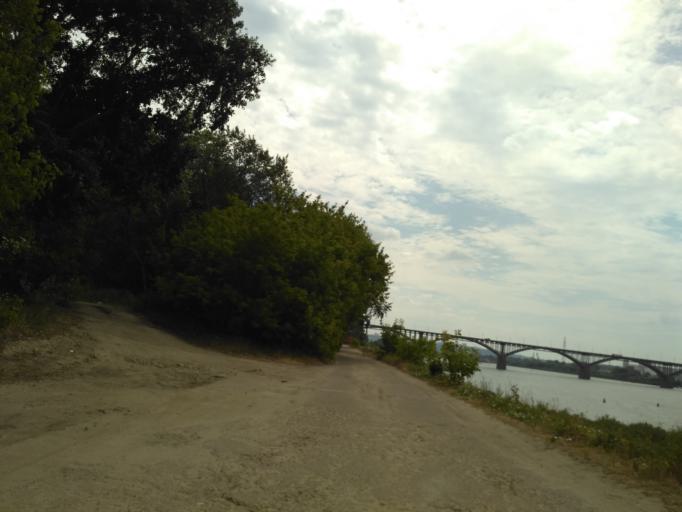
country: RU
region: Nizjnij Novgorod
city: Nizhniy Novgorod
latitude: 56.3076
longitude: 43.9680
